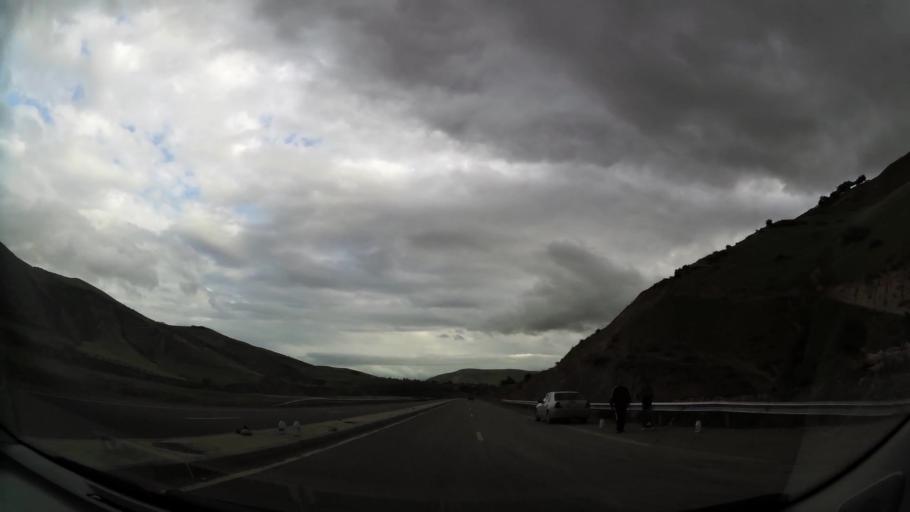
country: MA
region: Taza-Al Hoceima-Taounate
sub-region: Taza
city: Taza
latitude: 34.3201
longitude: -3.9578
